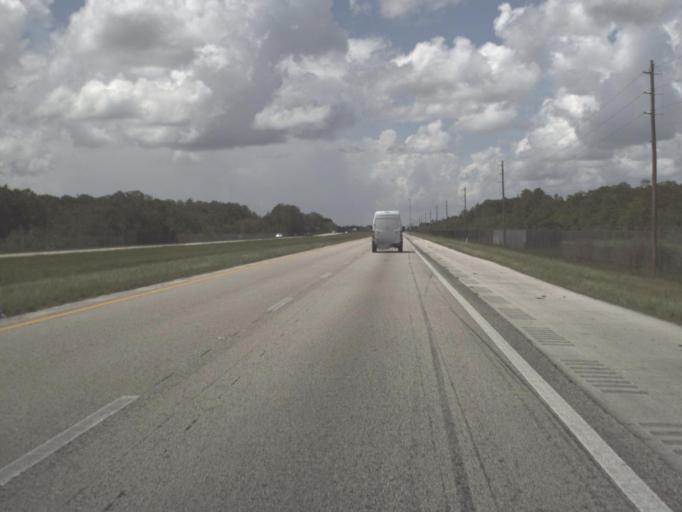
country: US
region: Florida
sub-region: Broward County
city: Weston
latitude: 26.1721
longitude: -80.9183
